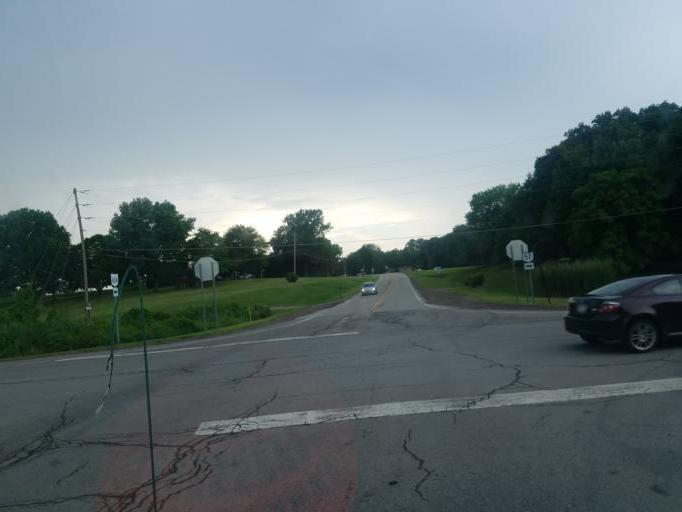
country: US
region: Ohio
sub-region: Wayne County
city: Rittman
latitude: 40.9460
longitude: -81.7634
